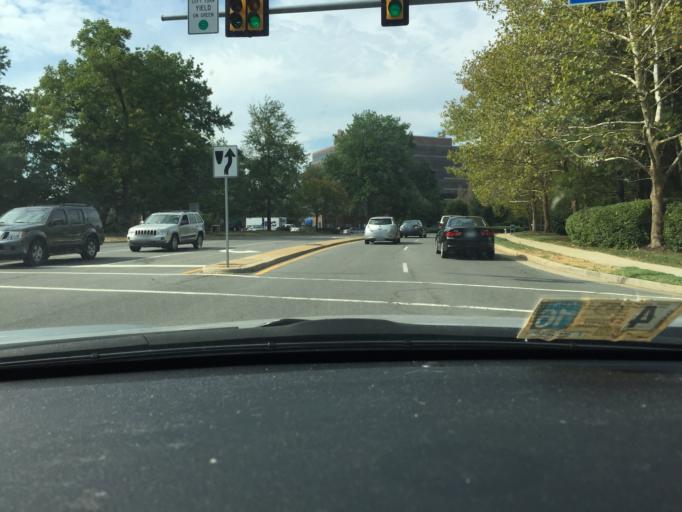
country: US
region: Virginia
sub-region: Fairfax County
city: Tysons Corner
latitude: 38.9124
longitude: -77.2276
